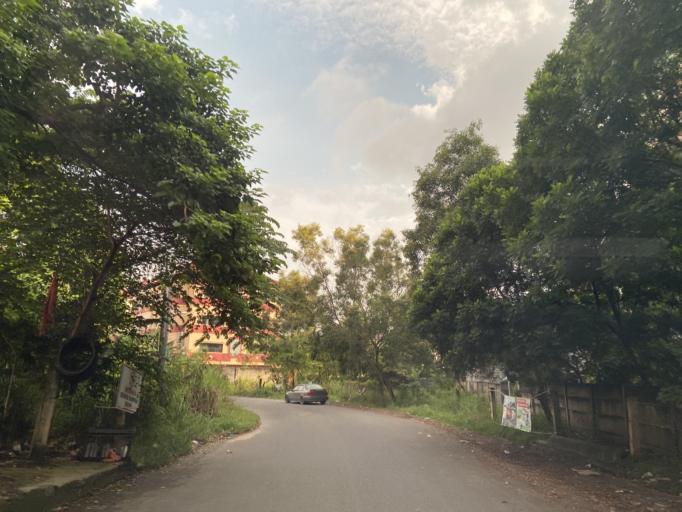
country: SG
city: Singapore
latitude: 1.1233
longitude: 104.0164
